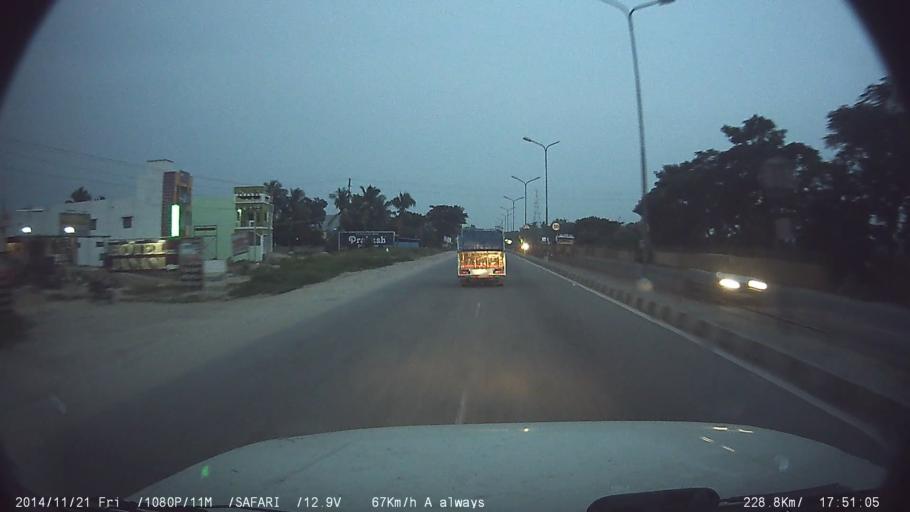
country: IN
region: Tamil Nadu
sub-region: Vellore
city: Walajapet
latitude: 12.9152
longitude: 79.3933
